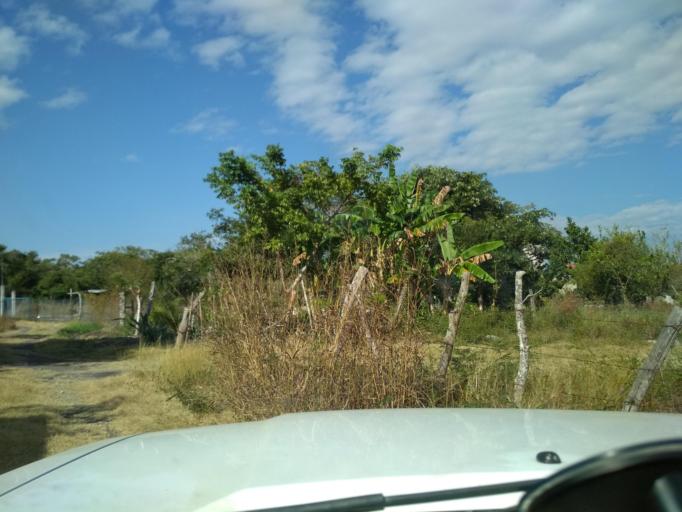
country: MX
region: Veracruz
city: Rinconada
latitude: 19.3590
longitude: -96.5595
